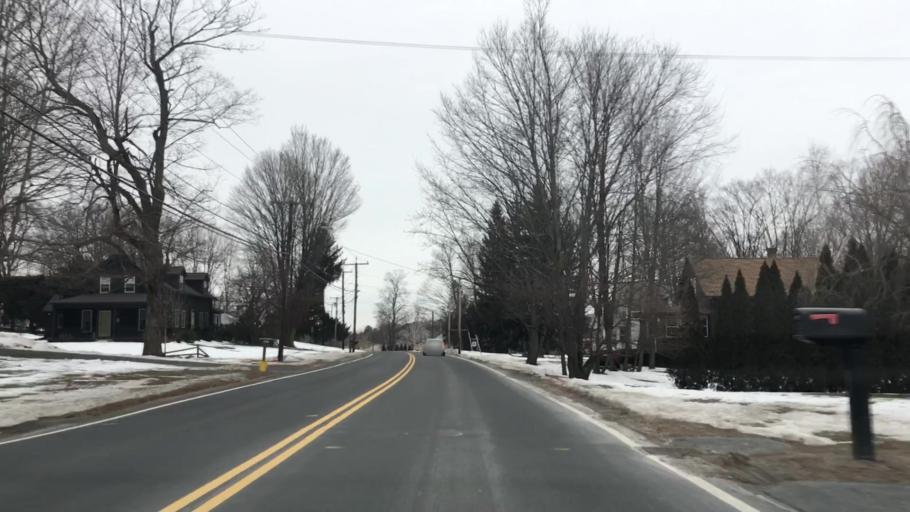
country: US
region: Massachusetts
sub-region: Hampden County
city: West Springfield
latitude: 42.0842
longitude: -72.6800
